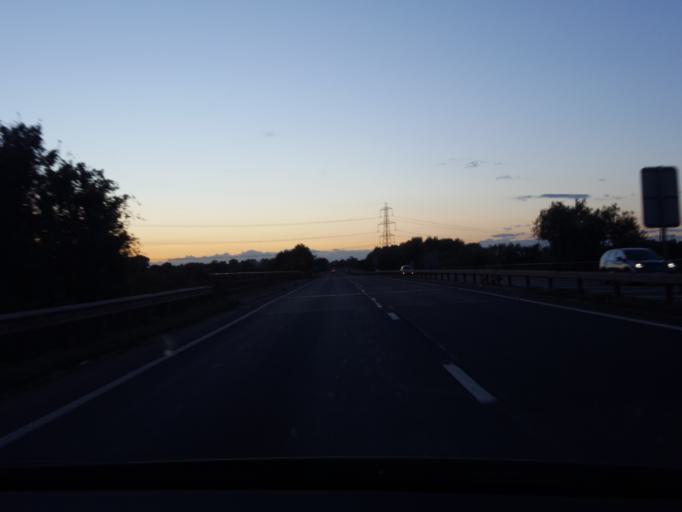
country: GB
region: England
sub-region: Leicestershire
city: Barrow upon Soar
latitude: 52.7417
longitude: -1.1471
